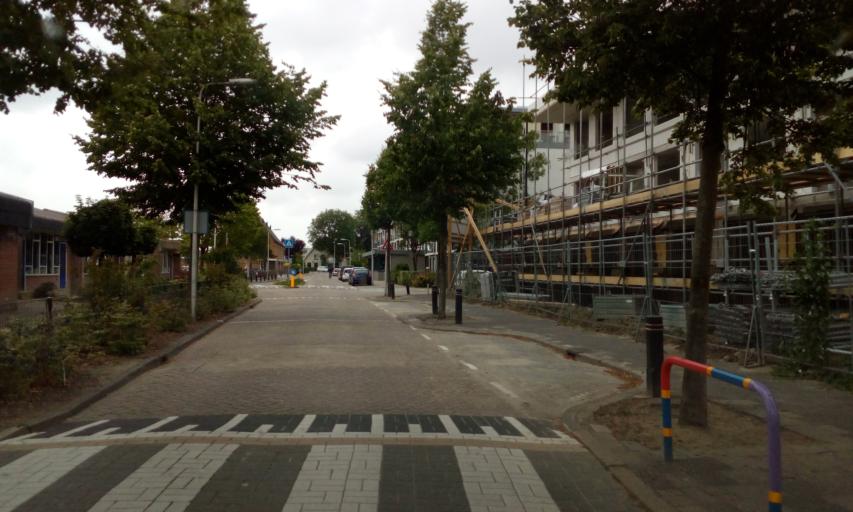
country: NL
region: South Holland
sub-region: Gemeente Westland
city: Kwintsheul
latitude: 52.0122
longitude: 4.2537
